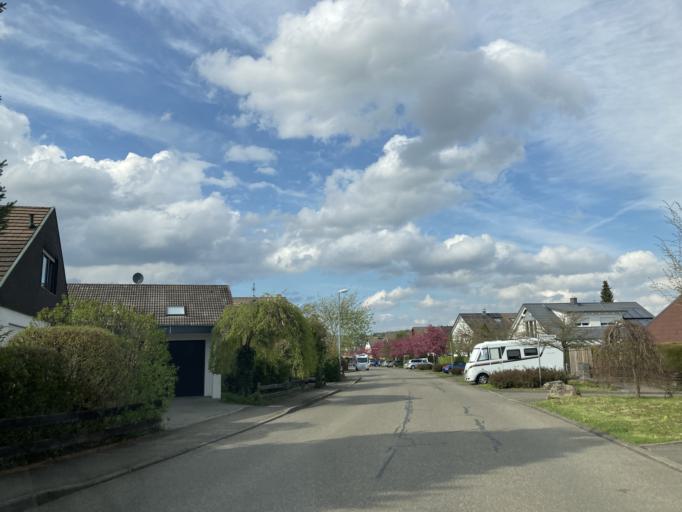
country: DE
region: Baden-Wuerttemberg
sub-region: Tuebingen Region
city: Dettenhausen
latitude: 48.6021
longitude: 9.1038
